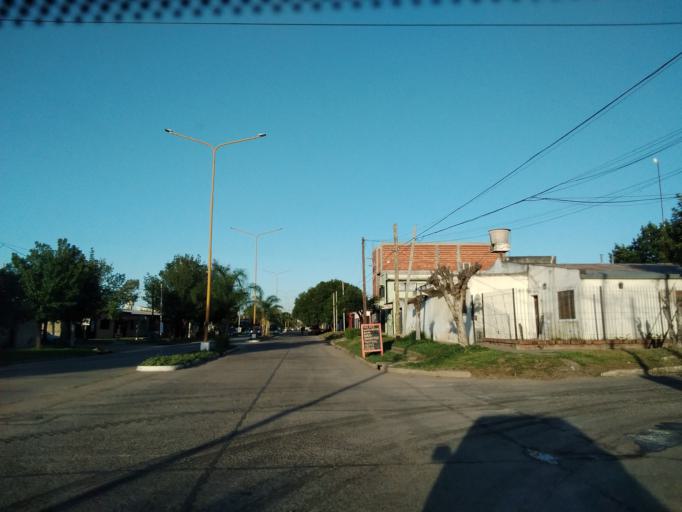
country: AR
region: Corrientes
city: Corrientes
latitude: -27.4613
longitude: -58.7840
